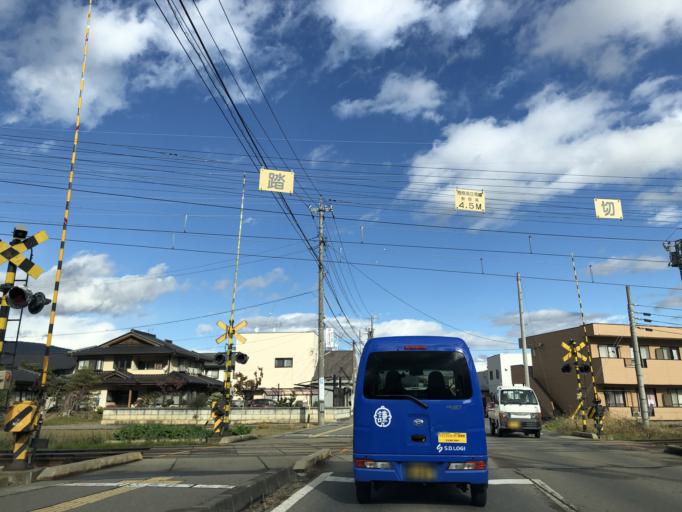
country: JP
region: Nagano
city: Suzaka
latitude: 36.6631
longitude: 138.2572
